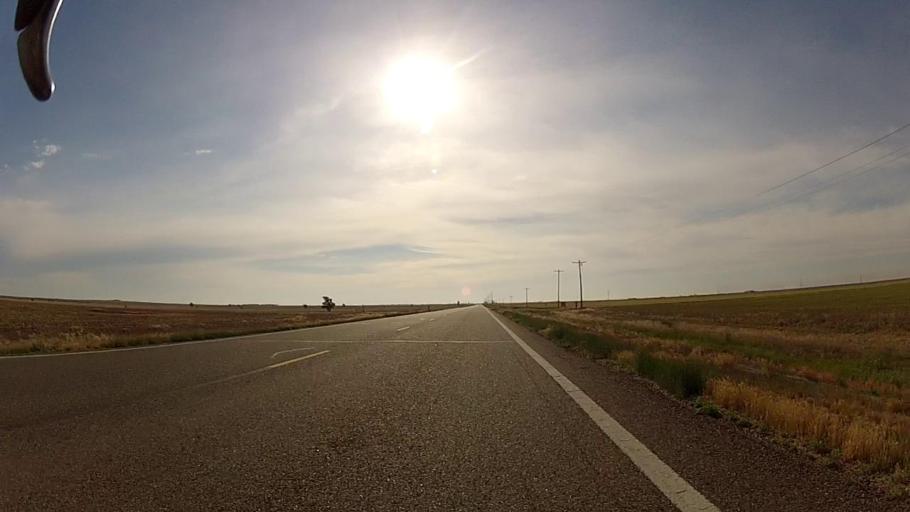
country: US
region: Kansas
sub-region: Grant County
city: Ulysses
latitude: 37.5766
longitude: -101.4454
